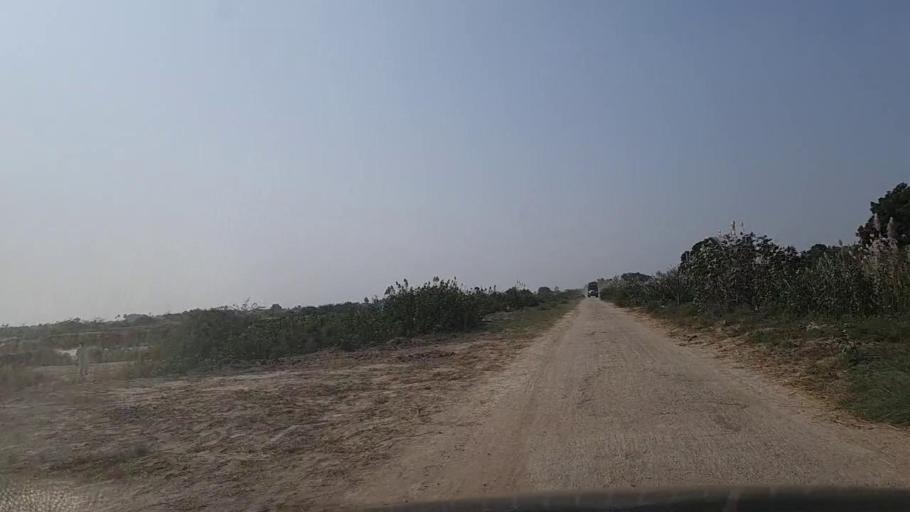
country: PK
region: Sindh
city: Gharo
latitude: 24.7096
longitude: 67.6512
